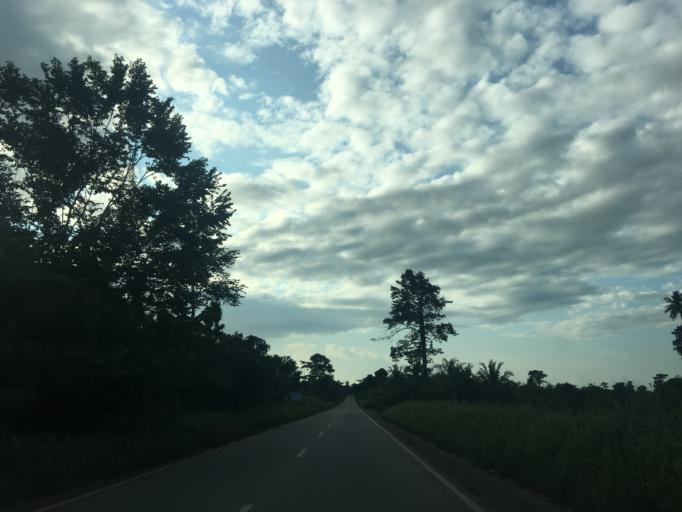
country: GH
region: Western
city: Bibiani
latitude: 6.3608
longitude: -2.2849
